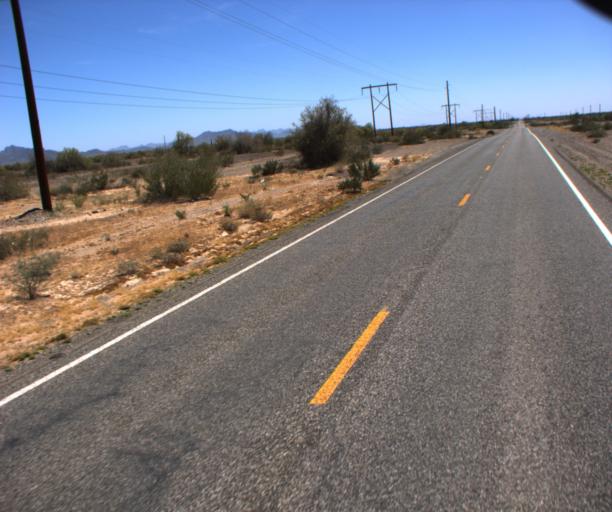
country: US
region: Arizona
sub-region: La Paz County
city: Quartzsite
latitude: 33.7060
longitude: -114.2171
